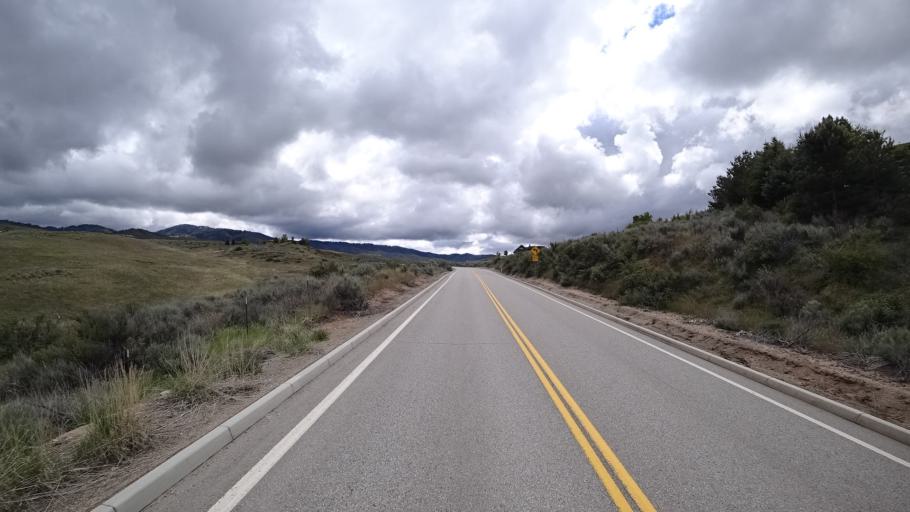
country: US
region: Idaho
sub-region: Ada County
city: Boise
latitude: 43.6941
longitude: -116.1763
